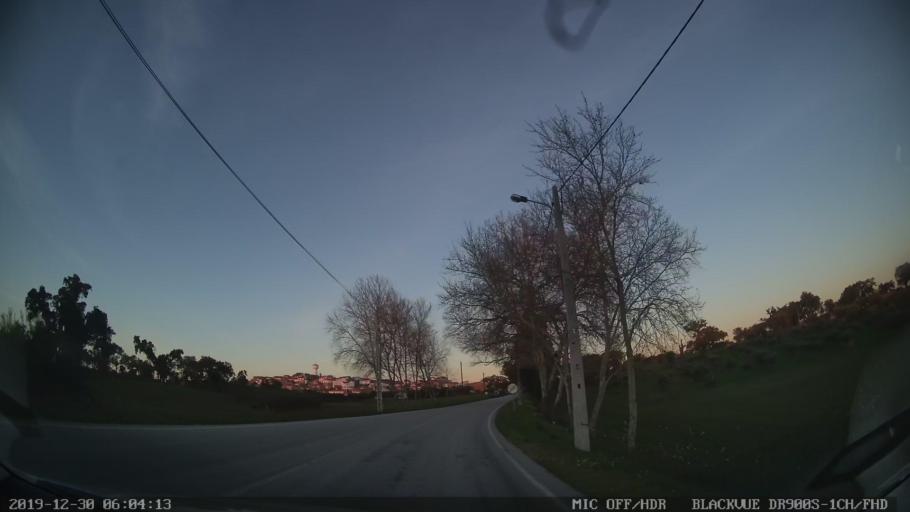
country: PT
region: Castelo Branco
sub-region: Penamacor
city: Penamacor
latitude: 40.0826
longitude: -7.2394
